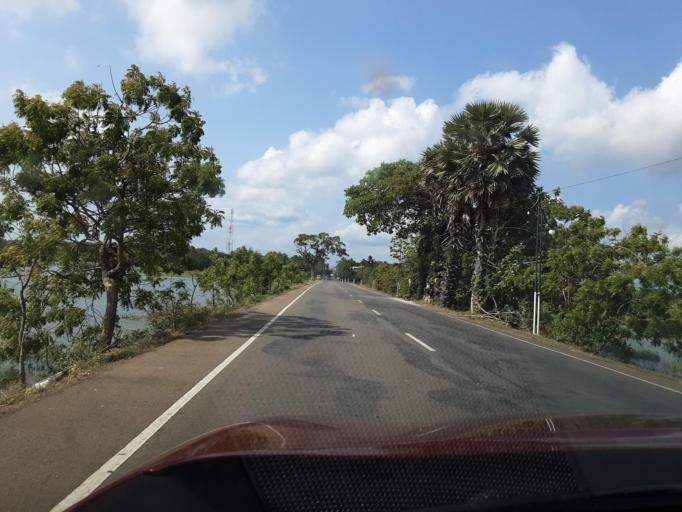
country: LK
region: Southern
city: Tangalla
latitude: 6.2914
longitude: 81.2350
